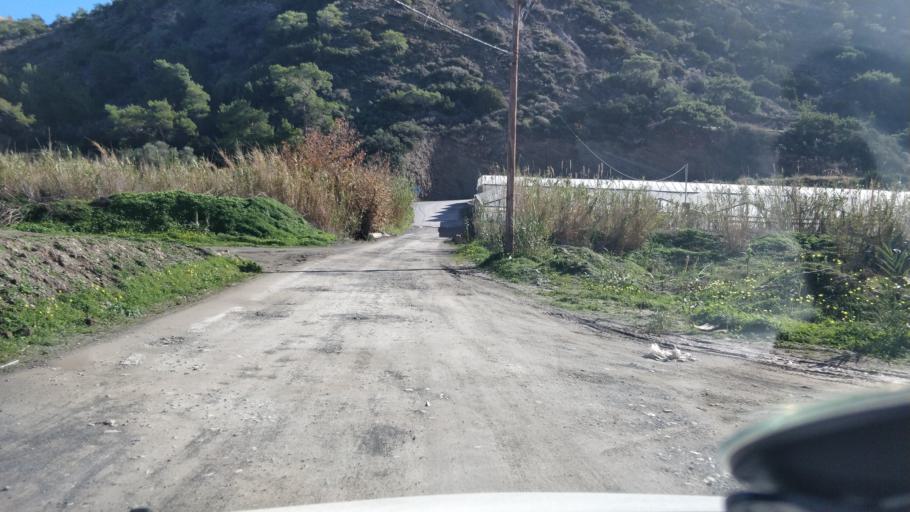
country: GR
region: Crete
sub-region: Nomos Lasithiou
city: Gra Liyia
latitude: 34.9905
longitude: 25.4837
